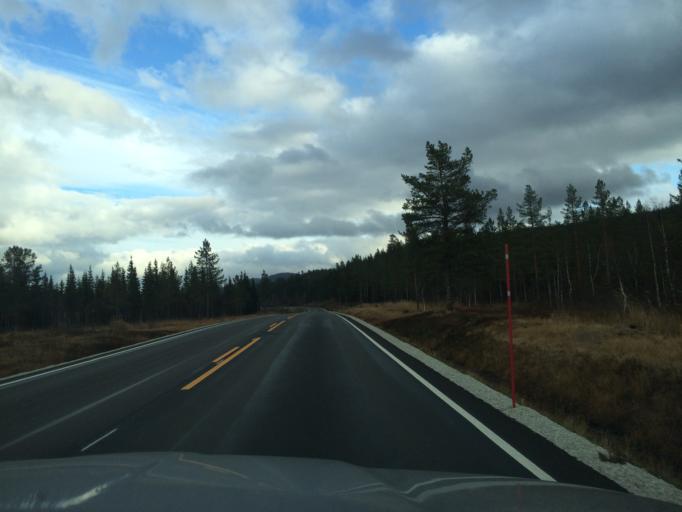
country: NO
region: Nord-Trondelag
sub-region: Namsskogan
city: Namsskogan
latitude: 64.7870
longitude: 12.9032
